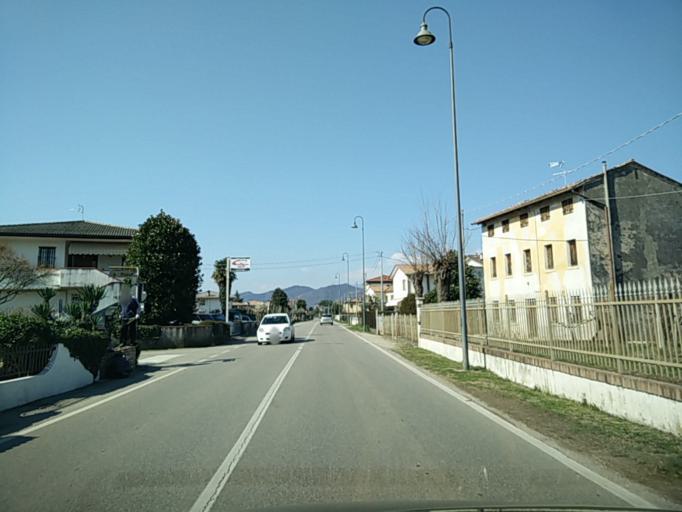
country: IT
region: Veneto
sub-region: Provincia di Treviso
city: Ciano
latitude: 45.8256
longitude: 12.0492
